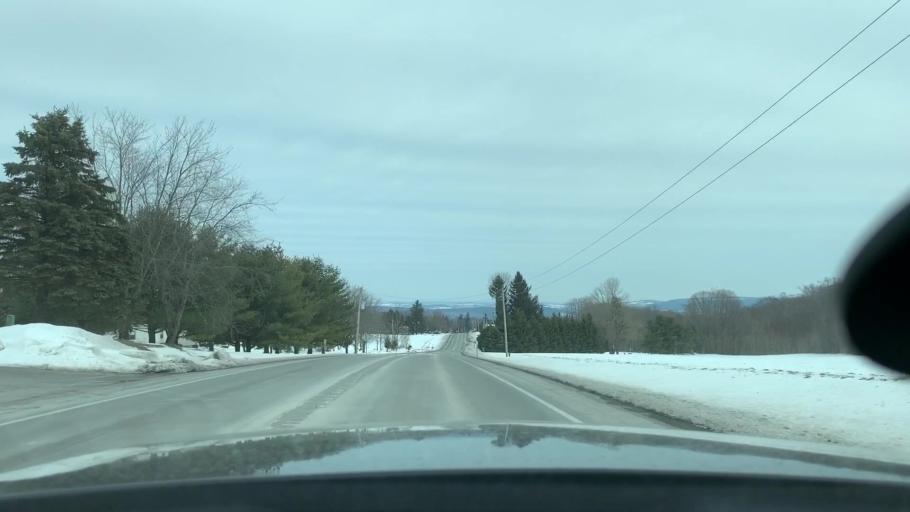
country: US
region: New York
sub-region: Herkimer County
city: Frankfort
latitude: 43.0303
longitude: -75.1624
